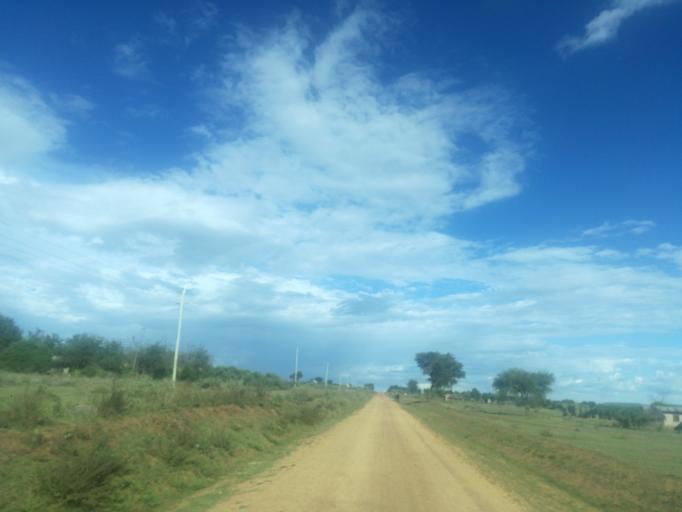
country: TZ
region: Mara
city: Issenye
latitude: -1.7545
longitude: 34.2565
